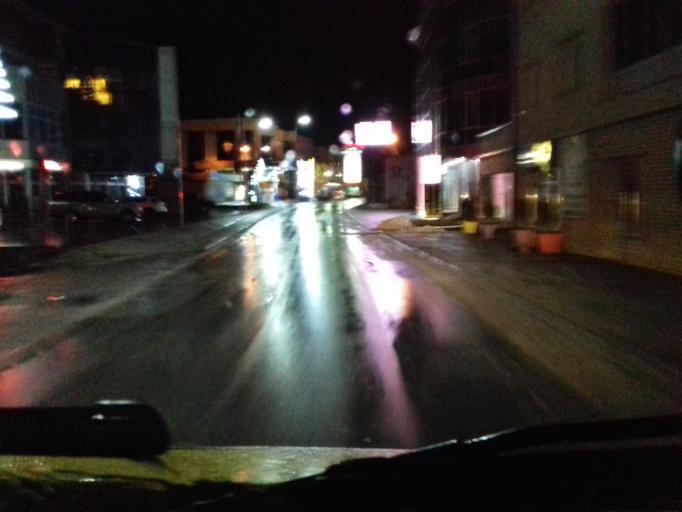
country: BA
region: Federation of Bosnia and Herzegovina
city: Kiseljak
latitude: 43.9407
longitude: 18.0792
